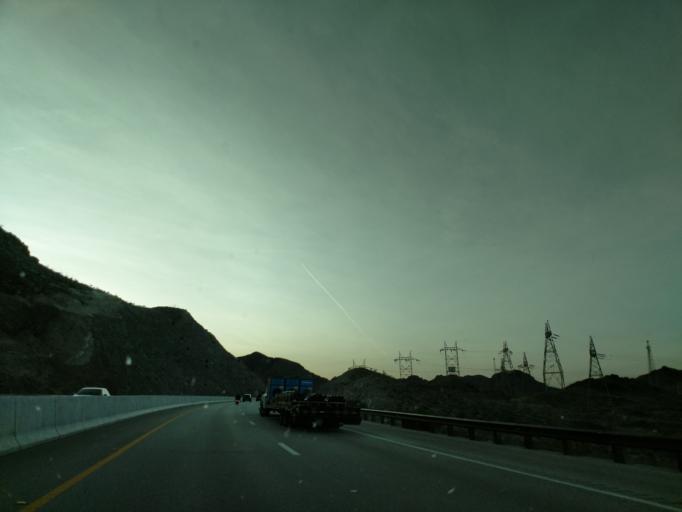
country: US
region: Nevada
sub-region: Clark County
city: Boulder City
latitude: 36.0098
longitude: -114.7351
